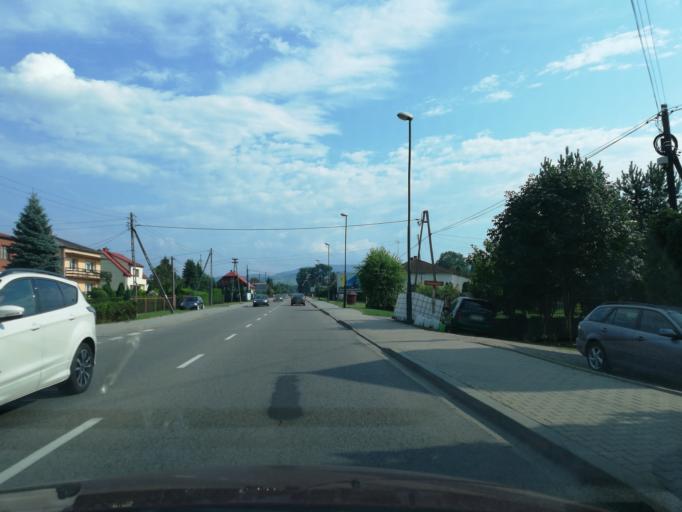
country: PL
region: Lesser Poland Voivodeship
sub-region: Powiat nowosadecki
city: Nawojowa
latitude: 49.5784
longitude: 20.7299
